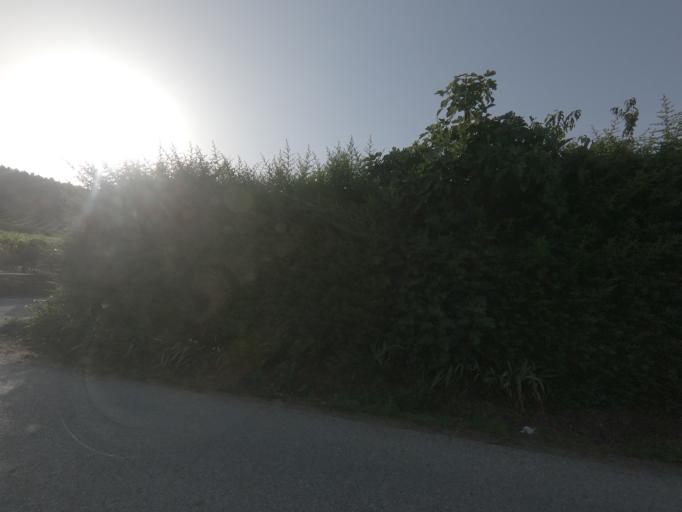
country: PT
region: Vila Real
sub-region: Sabrosa
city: Sabrosa
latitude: 41.2516
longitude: -7.4657
